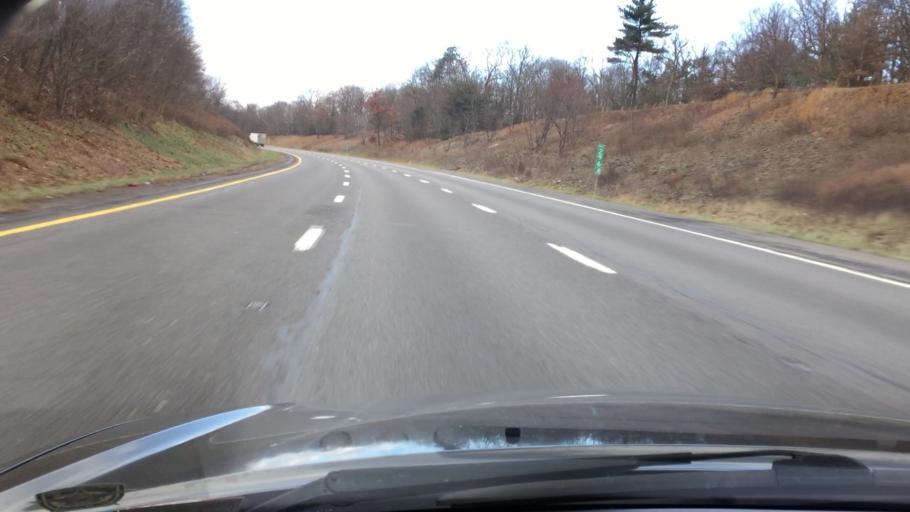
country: US
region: Pennsylvania
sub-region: Monroe County
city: Tannersville
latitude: 41.0609
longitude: -75.3294
